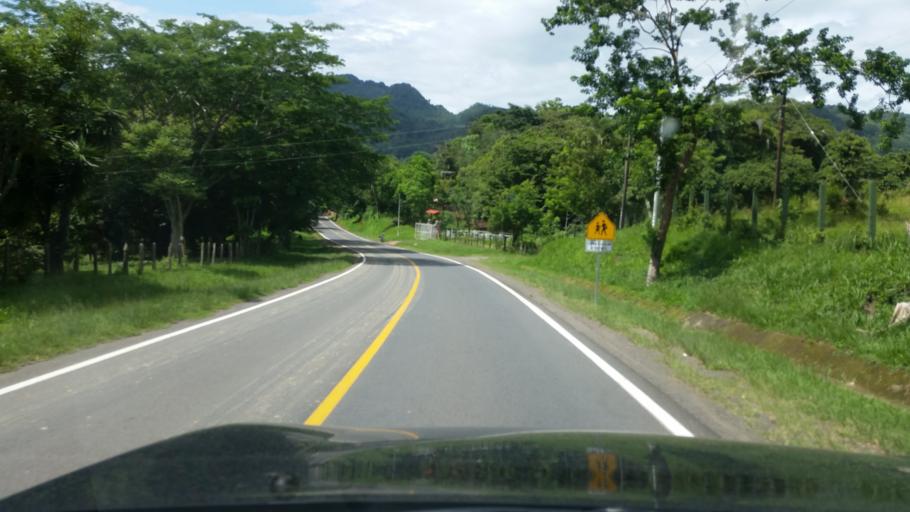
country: NI
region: Matagalpa
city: San Ramon
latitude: 12.9455
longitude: -85.8737
